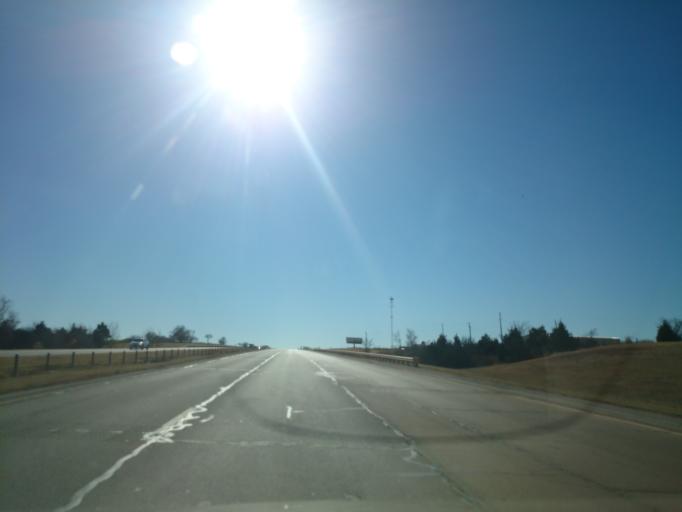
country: US
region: Oklahoma
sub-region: Logan County
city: Guthrie
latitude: 35.8723
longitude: -97.3943
